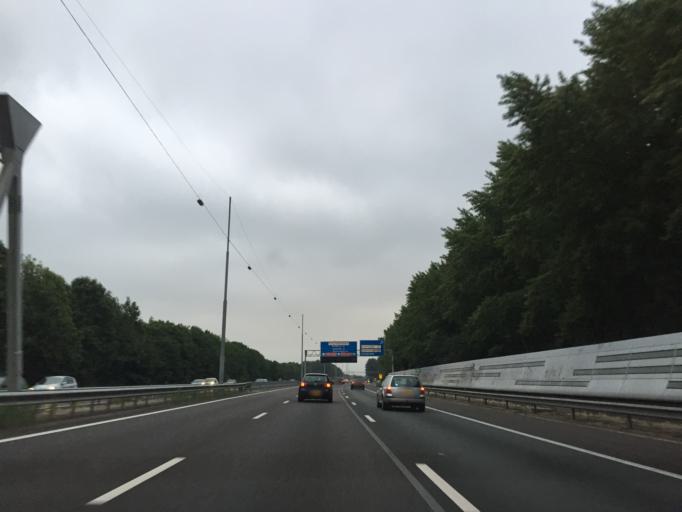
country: NL
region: North Holland
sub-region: Gemeente Waterland
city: Broek in Waterland
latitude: 52.3961
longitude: 4.9613
